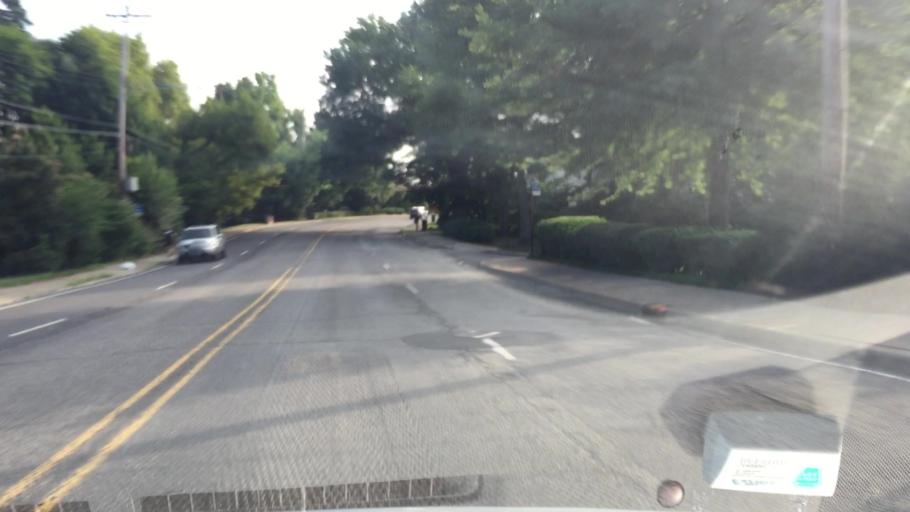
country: US
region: Pennsylvania
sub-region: Allegheny County
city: Heidelberg
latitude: 40.3731
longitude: -80.0758
